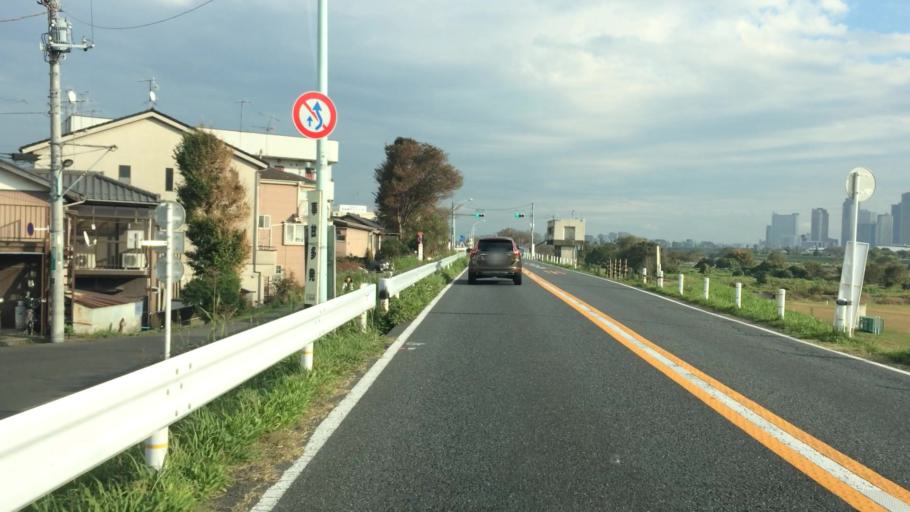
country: JP
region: Tokyo
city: Tokyo
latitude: 35.5995
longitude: 139.6438
